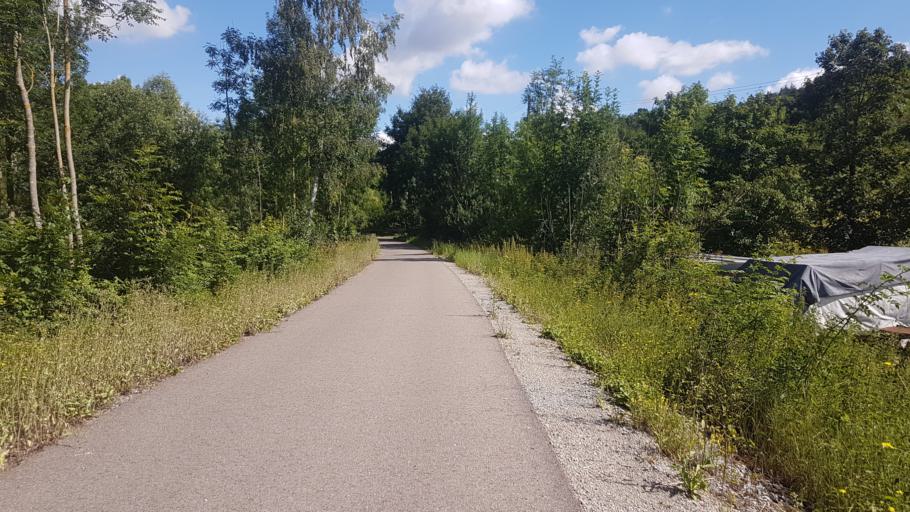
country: DE
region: Bavaria
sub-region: Regierungsbezirk Unterfranken
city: Bieberehren
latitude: 49.5037
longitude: 10.0194
